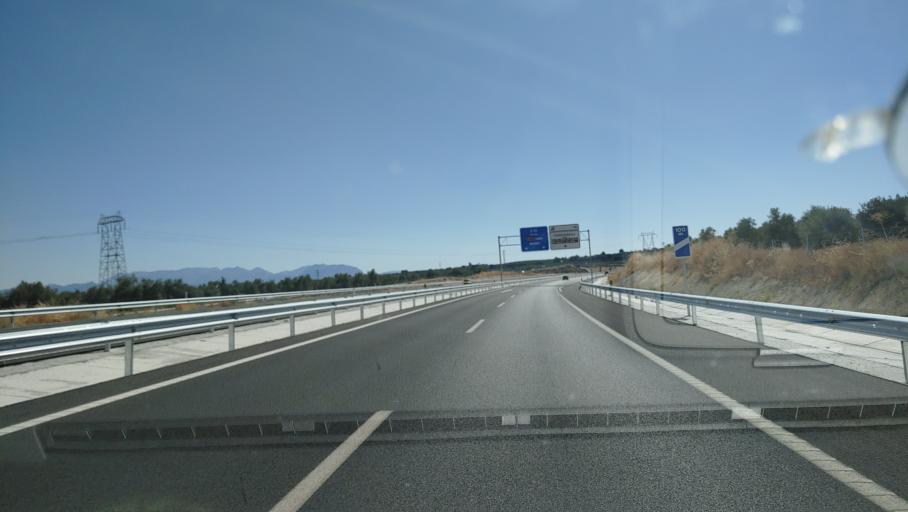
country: ES
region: Andalusia
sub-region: Provincia de Jaen
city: Sabiote
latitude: 38.0358
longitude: -3.3265
